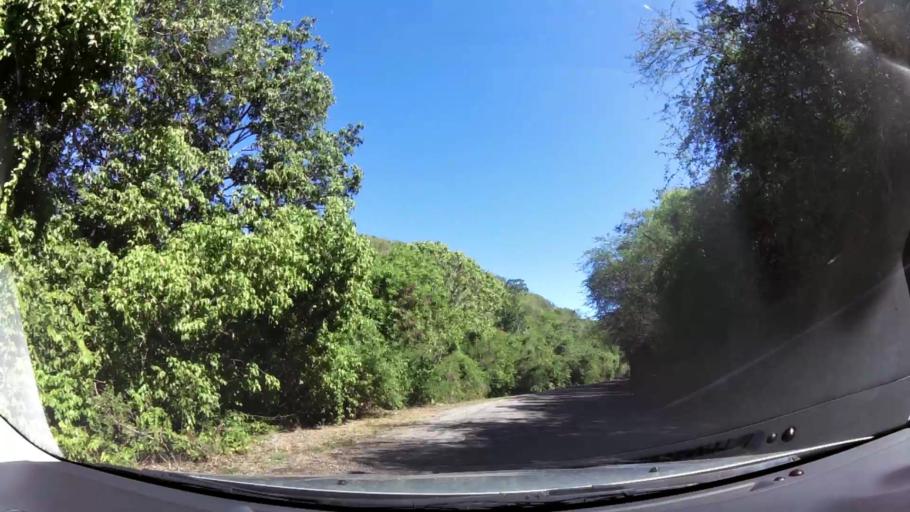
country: AG
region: Saint Paul
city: Falmouth
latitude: 17.0073
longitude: -61.7585
